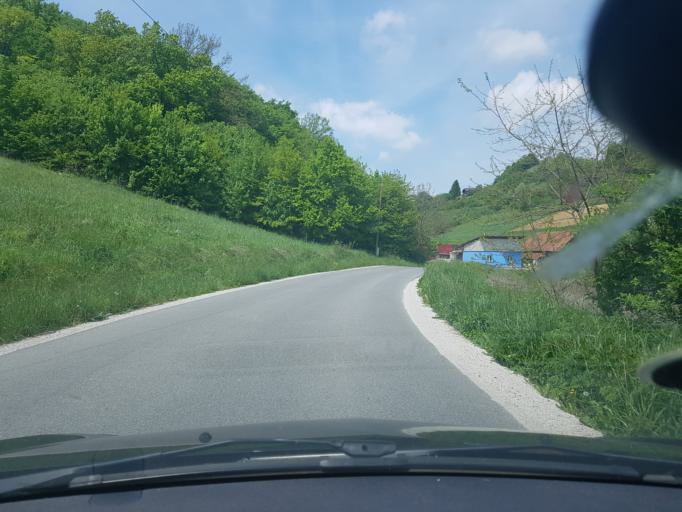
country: HR
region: Krapinsko-Zagorska
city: Pregrada
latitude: 46.1904
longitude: 15.7221
